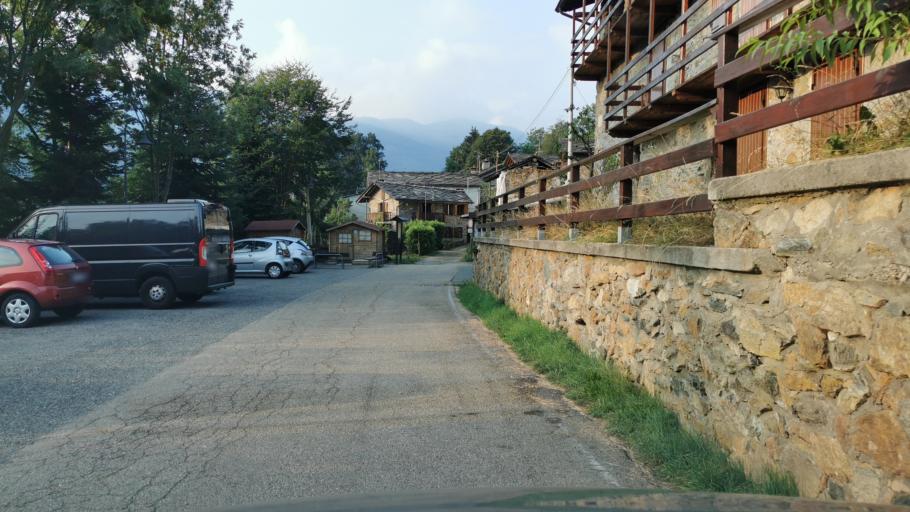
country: IT
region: Piedmont
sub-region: Provincia di Torino
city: La Villa
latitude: 45.2589
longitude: 7.4331
